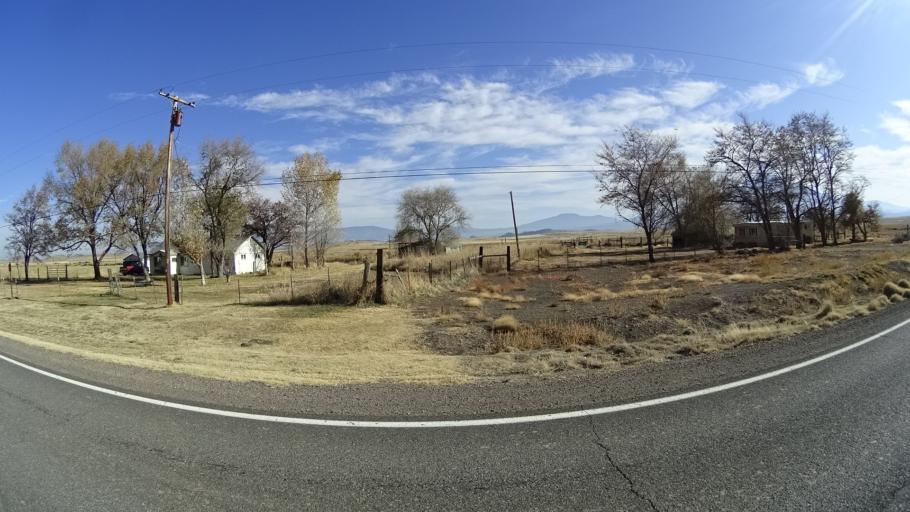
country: US
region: California
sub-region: Siskiyou County
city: Weed
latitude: 41.5011
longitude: -122.5144
